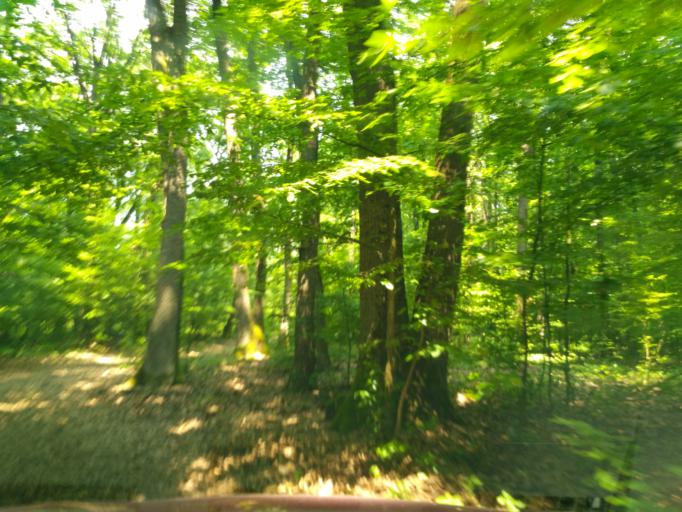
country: SK
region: Kosicky
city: Moldava nad Bodvou
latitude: 48.6405
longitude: 21.0395
